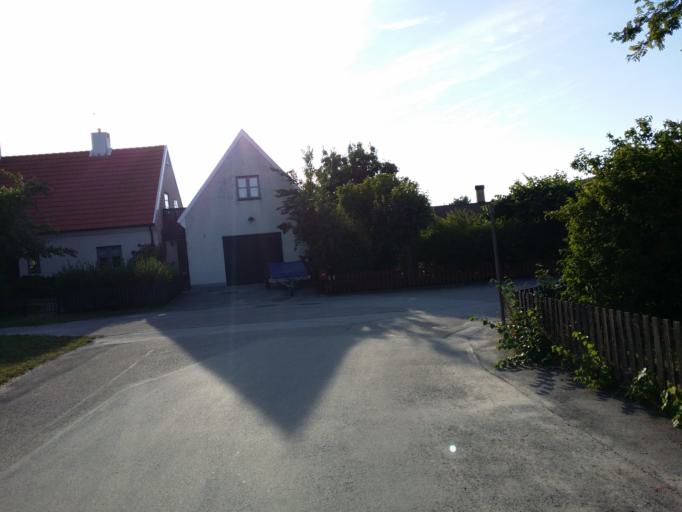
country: SE
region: Gotland
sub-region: Gotland
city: Visby
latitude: 57.6342
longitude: 18.3202
